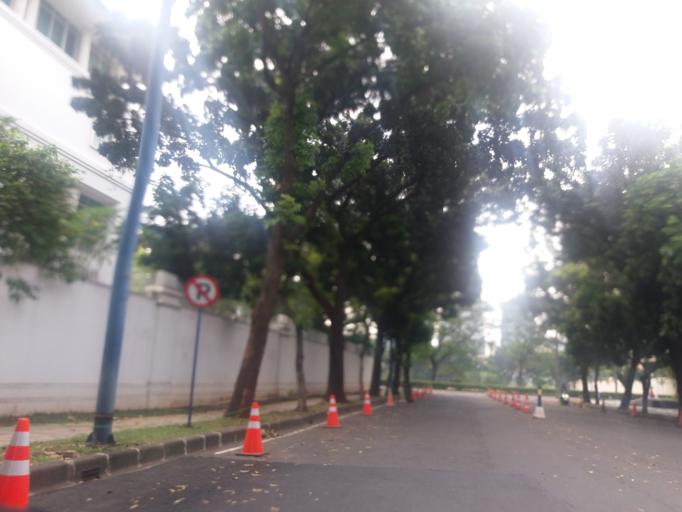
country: ID
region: Jakarta Raya
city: Jakarta
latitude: -6.2322
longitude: 106.8283
